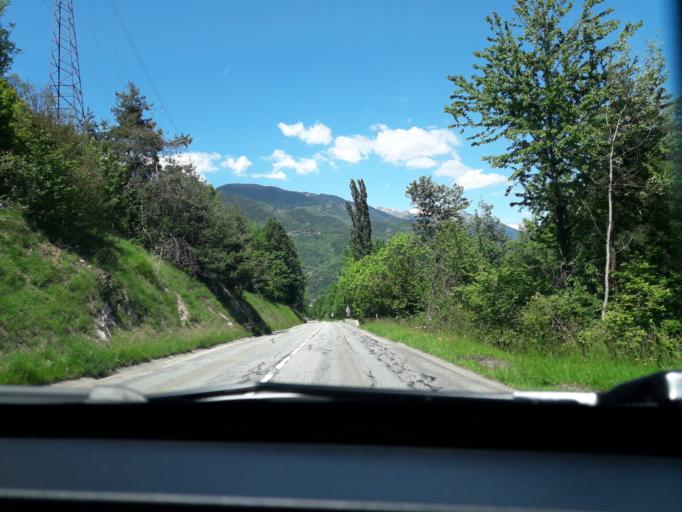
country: FR
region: Rhone-Alpes
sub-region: Departement de la Savoie
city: Salins-les-Thermes
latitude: 45.4683
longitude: 6.5240
